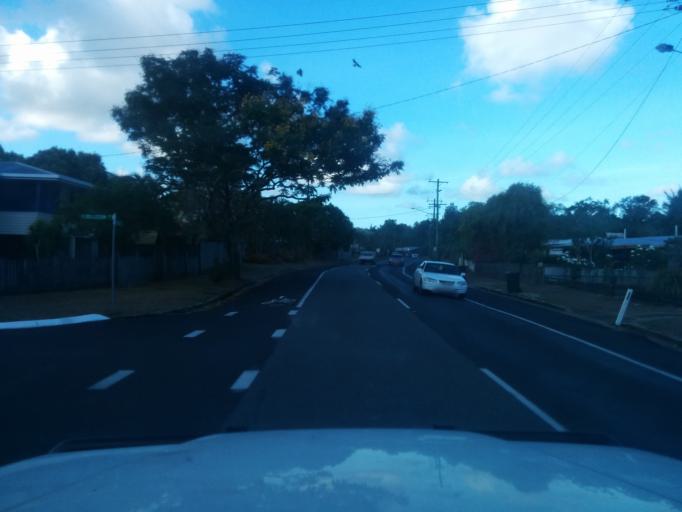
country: AU
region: Queensland
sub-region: Cairns
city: Cairns
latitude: -16.9204
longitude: 145.7467
